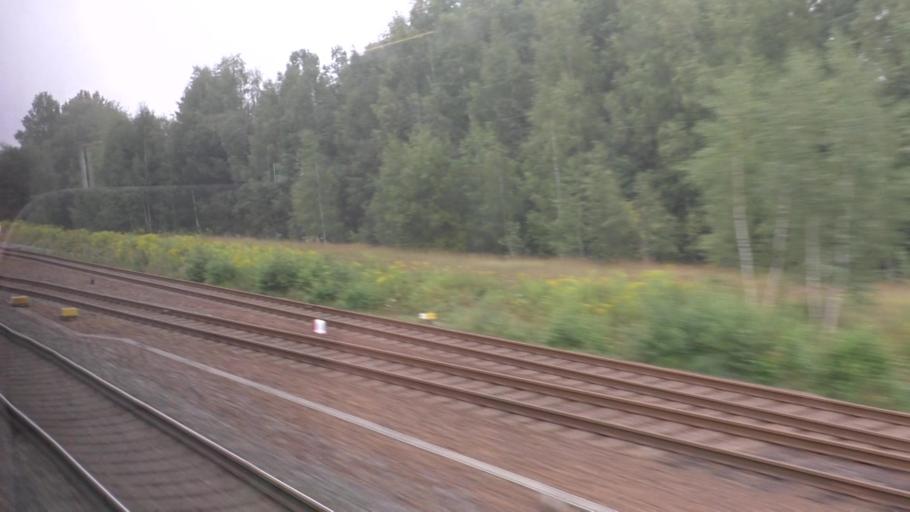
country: DE
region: Saxony
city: Arnsdorf
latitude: 51.0946
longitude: 13.9769
